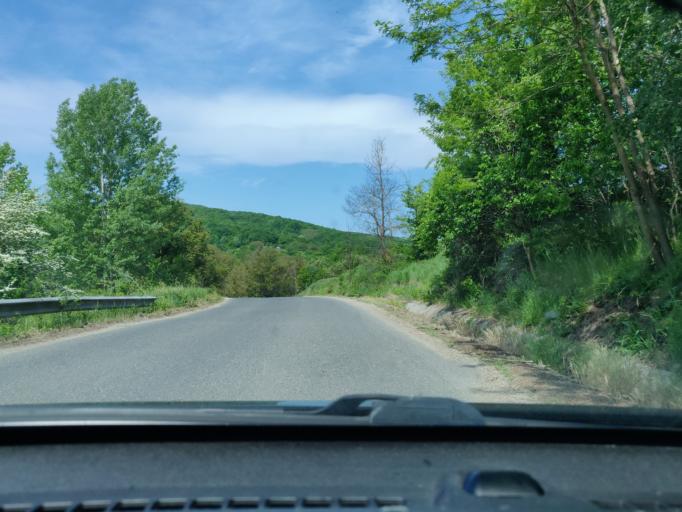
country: RO
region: Vrancea
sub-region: Comuna Vidra
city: Vidra
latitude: 45.9335
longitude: 26.8840
